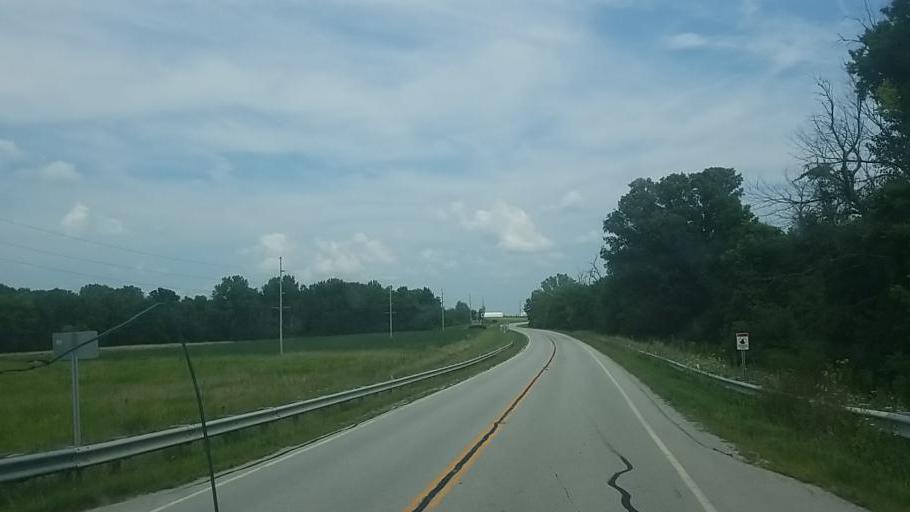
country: US
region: Ohio
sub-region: Hardin County
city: Forest
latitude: 40.7821
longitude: -83.5750
